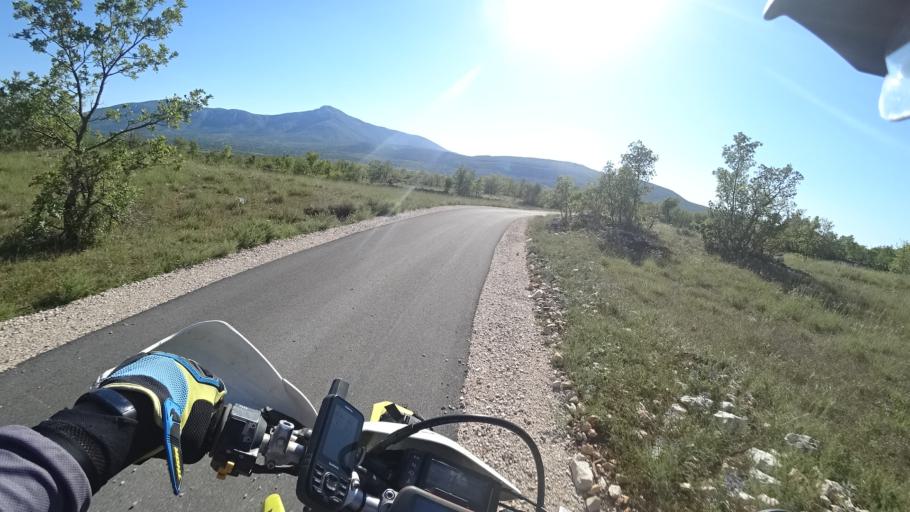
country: BA
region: Federation of Bosnia and Herzegovina
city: Bosansko Grahovo
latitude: 44.0068
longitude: 16.3696
